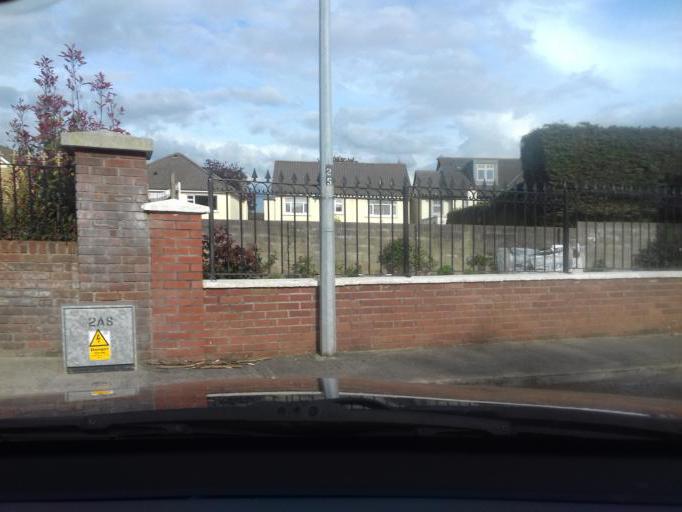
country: IE
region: Leinster
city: Castleknock
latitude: 53.3725
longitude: -6.3525
